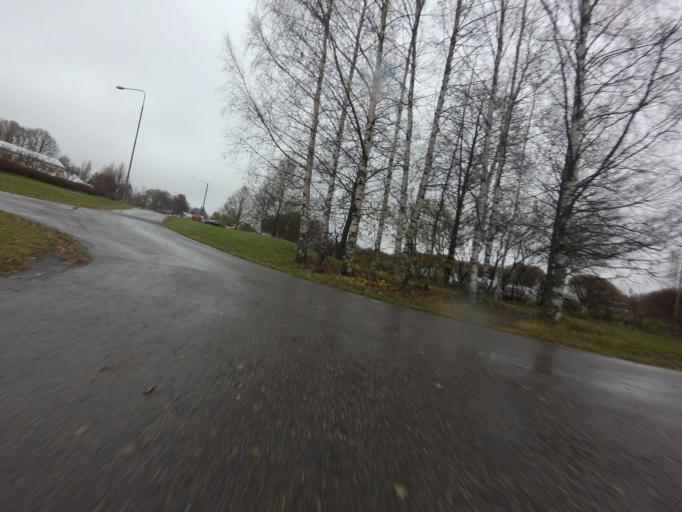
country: FI
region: Uusimaa
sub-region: Helsinki
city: Espoo
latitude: 60.2115
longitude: 24.6560
